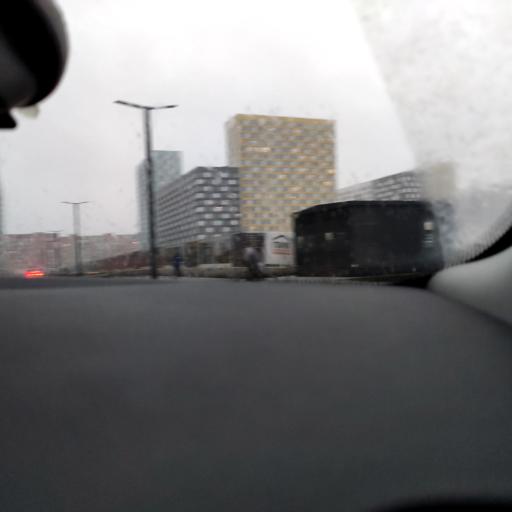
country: RU
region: Moskovskaya
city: Mytishchi
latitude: 55.9184
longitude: 37.7188
